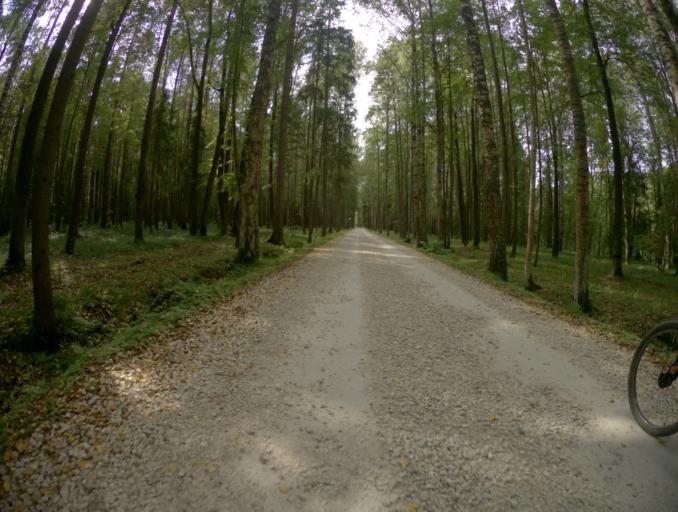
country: RU
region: Vladimir
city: Raduzhnyy
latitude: 56.0617
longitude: 40.2988
